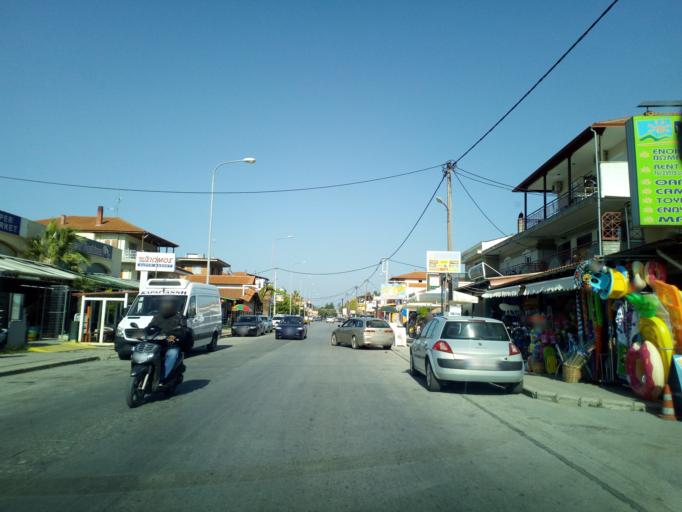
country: GR
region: Central Macedonia
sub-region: Nomos Thessalonikis
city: Stavros
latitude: 40.6653
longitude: 23.6921
